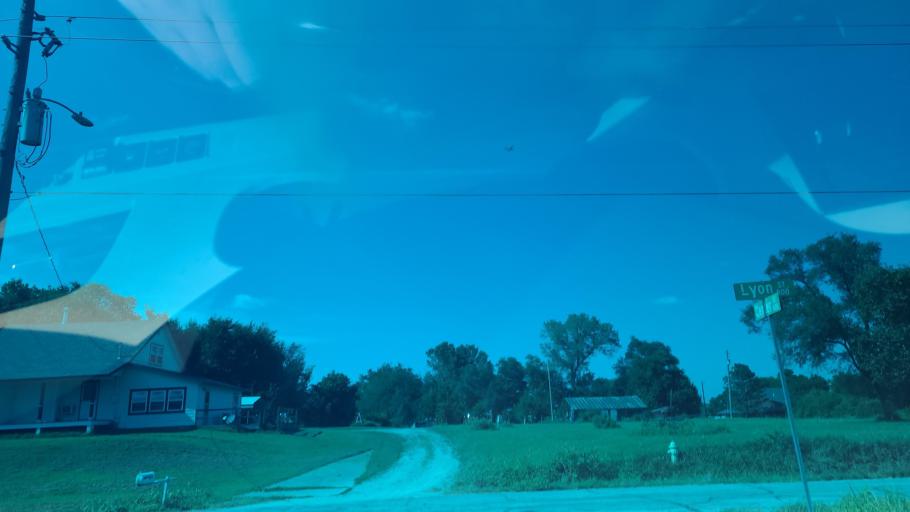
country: US
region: Kansas
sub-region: Douglas County
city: Lawrence
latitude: 38.9823
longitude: -95.2169
